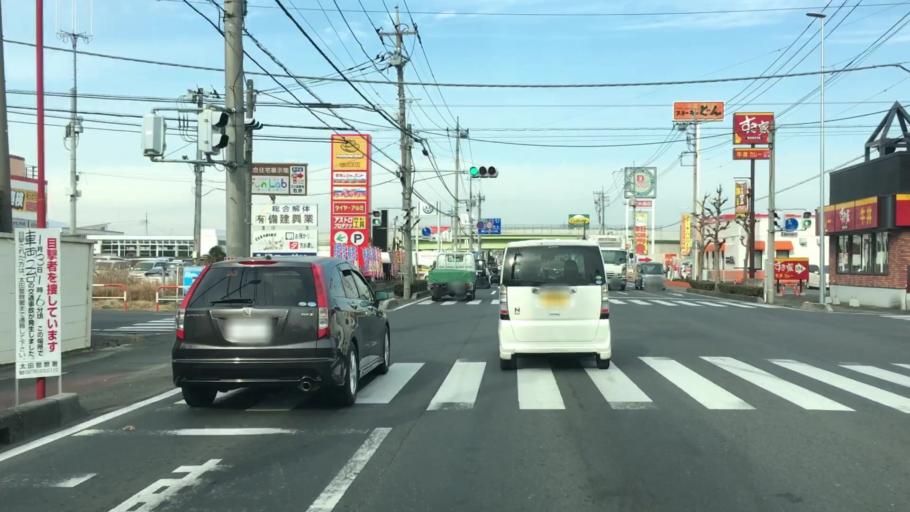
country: JP
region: Gunma
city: Ota
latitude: 36.2674
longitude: 139.3770
